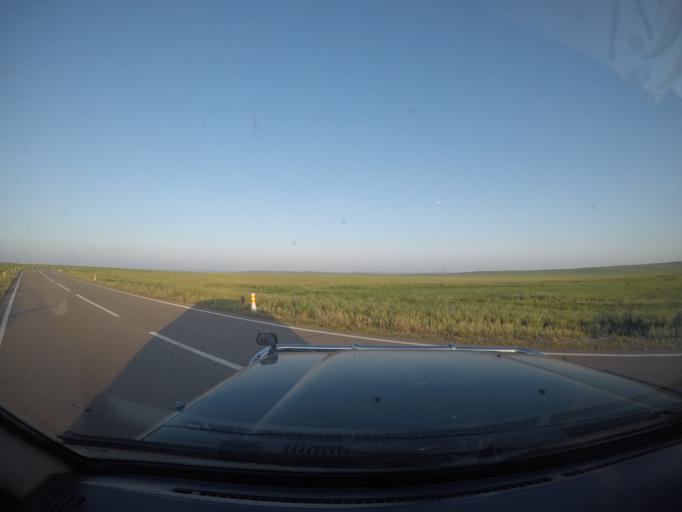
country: MN
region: Suhbaatar
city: Hanhohiy
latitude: 47.5731
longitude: 112.2266
